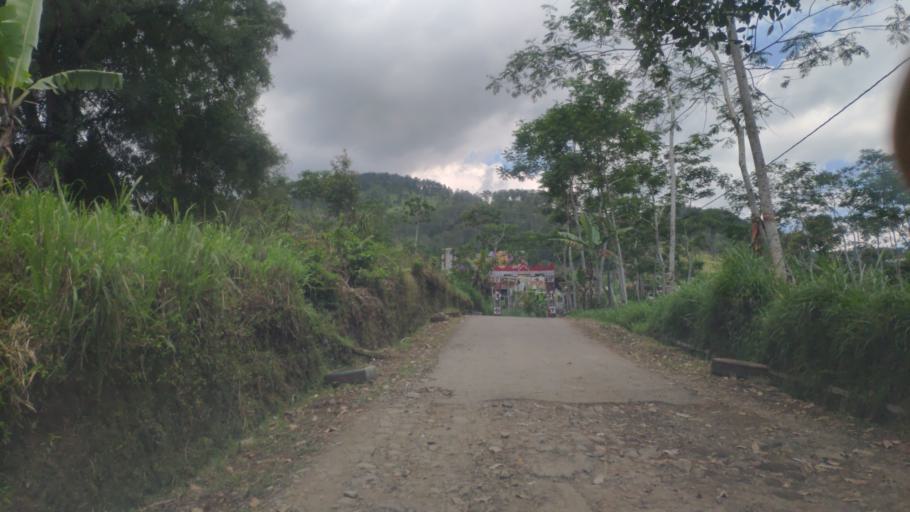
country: ID
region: Central Java
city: Buaran
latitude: -7.1889
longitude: 109.6743
